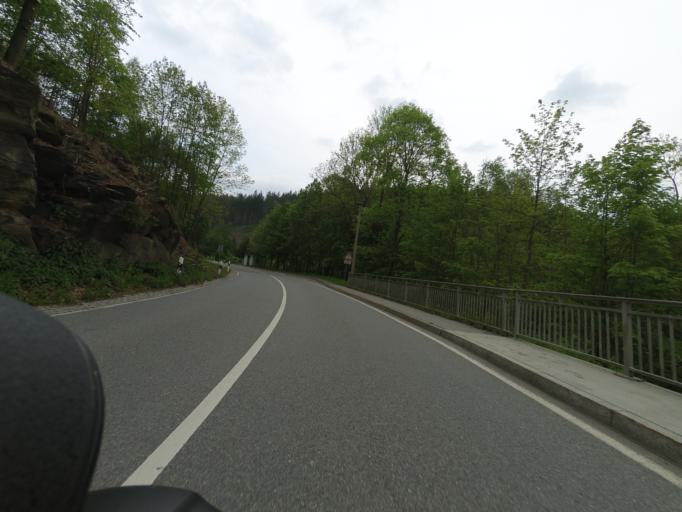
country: DE
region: Saxony
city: Wolkenstein
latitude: 50.6693
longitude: 13.0650
